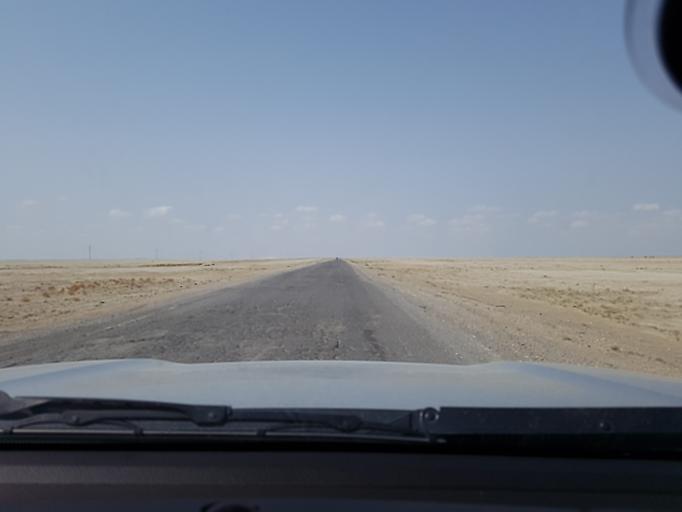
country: TM
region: Balkan
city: Gumdag
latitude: 38.6632
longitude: 54.3979
